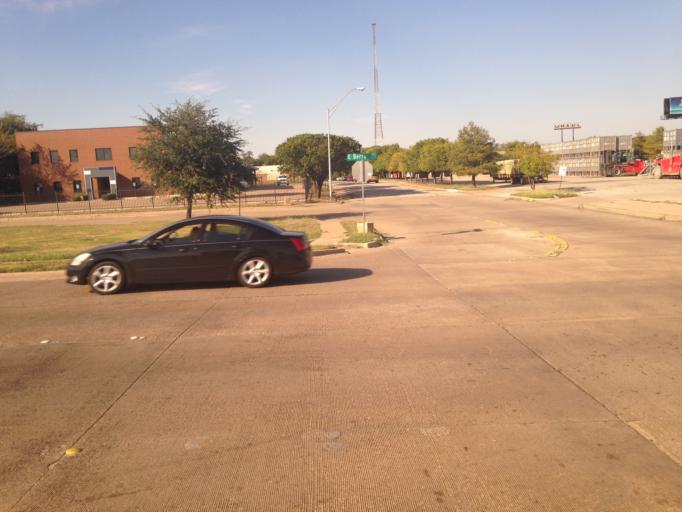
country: US
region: Texas
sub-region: Tarrant County
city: Fort Worth
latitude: 32.7059
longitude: -97.3224
